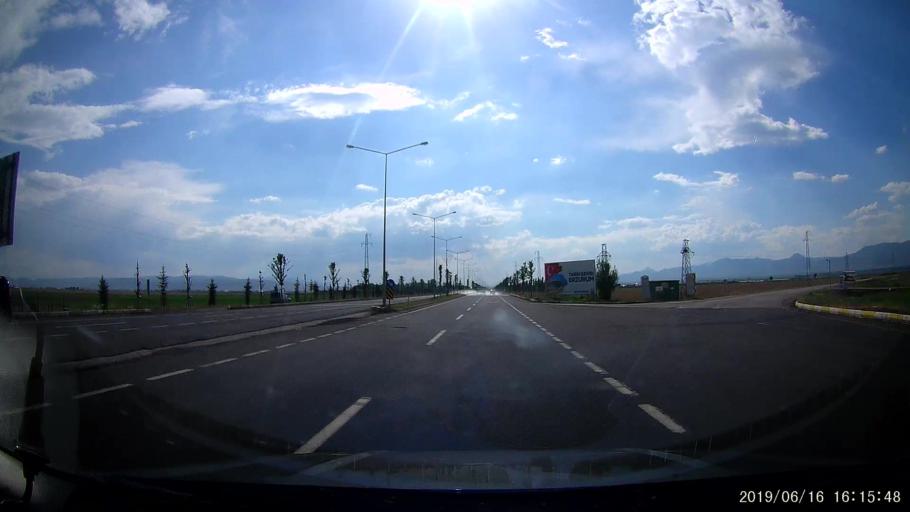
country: TR
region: Erzurum
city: Erzurum
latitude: 39.9623
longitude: 41.2184
